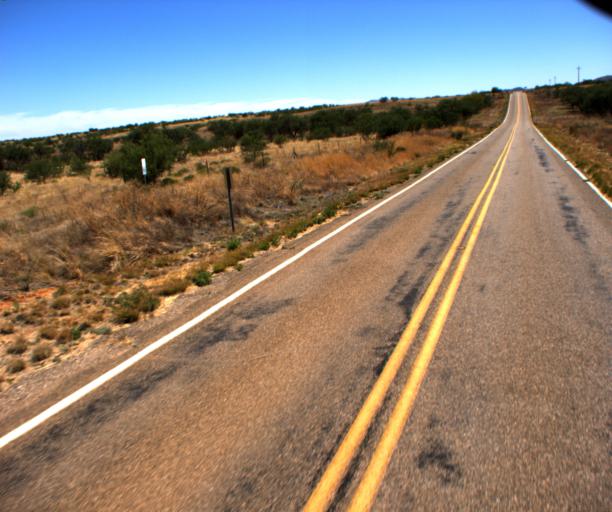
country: US
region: Arizona
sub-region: Pima County
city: Sells
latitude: 31.5942
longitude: -111.5286
